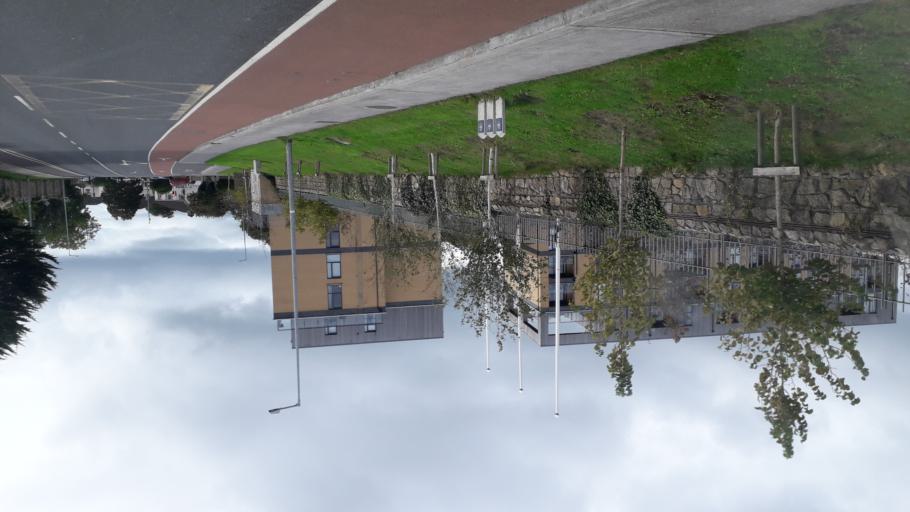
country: IE
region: Leinster
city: Cabinteely
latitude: 53.2681
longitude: -6.1495
